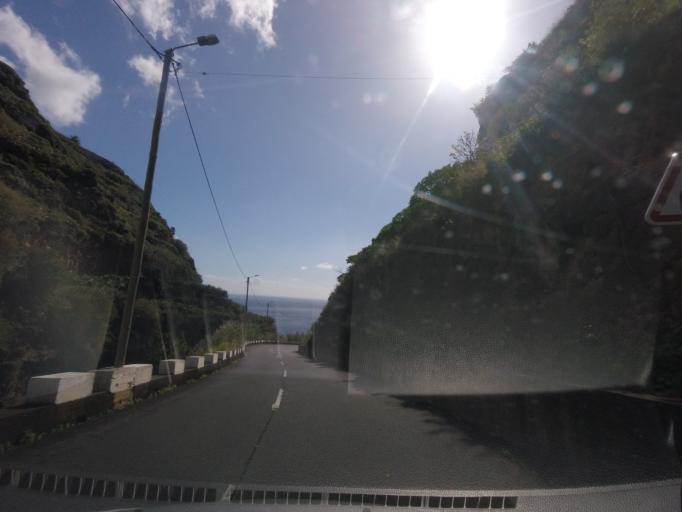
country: PT
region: Madeira
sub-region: Calheta
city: Estreito da Calheta
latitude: 32.7344
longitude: -17.2003
